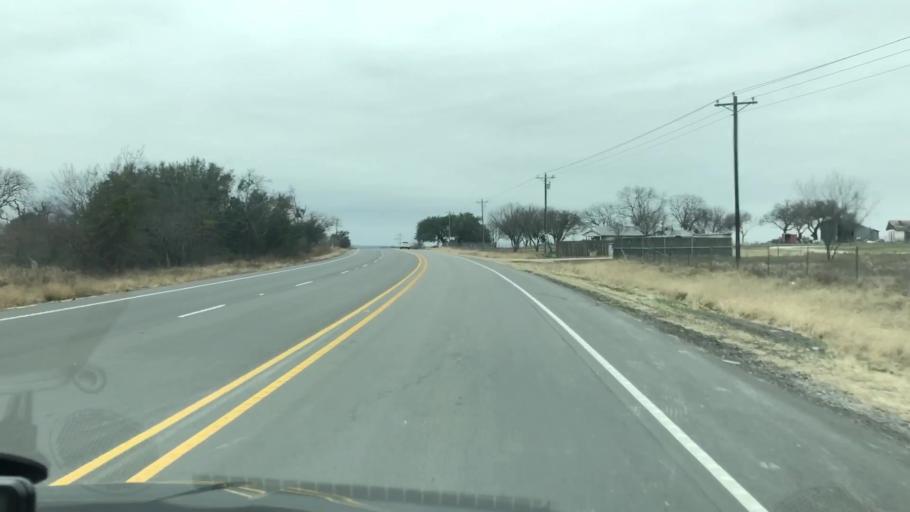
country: US
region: Texas
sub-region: Erath County
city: Stephenville
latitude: 32.1875
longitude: -98.1682
